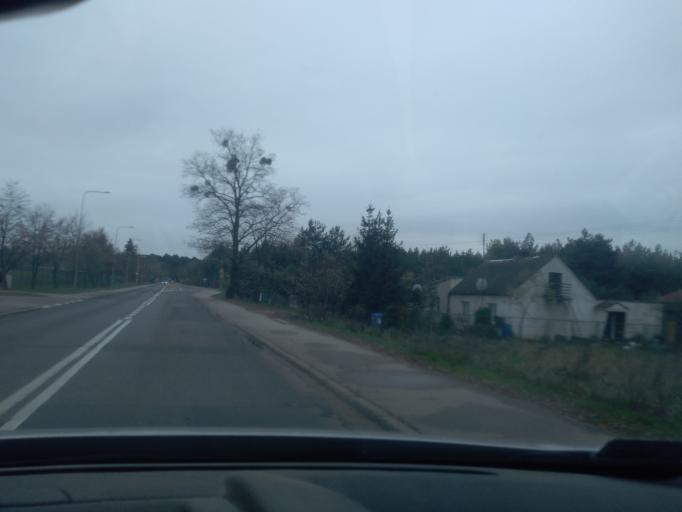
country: PL
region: Greater Poland Voivodeship
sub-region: Powiat poznanski
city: Murowana Goslina
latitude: 52.5446
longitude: 16.9727
